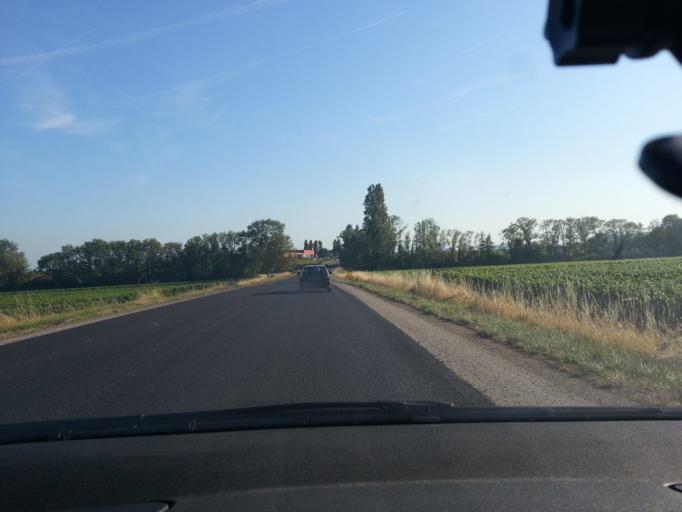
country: FR
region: Bourgogne
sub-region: Departement de la Cote-d'Or
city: Meursault
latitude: 46.9865
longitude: 4.7920
